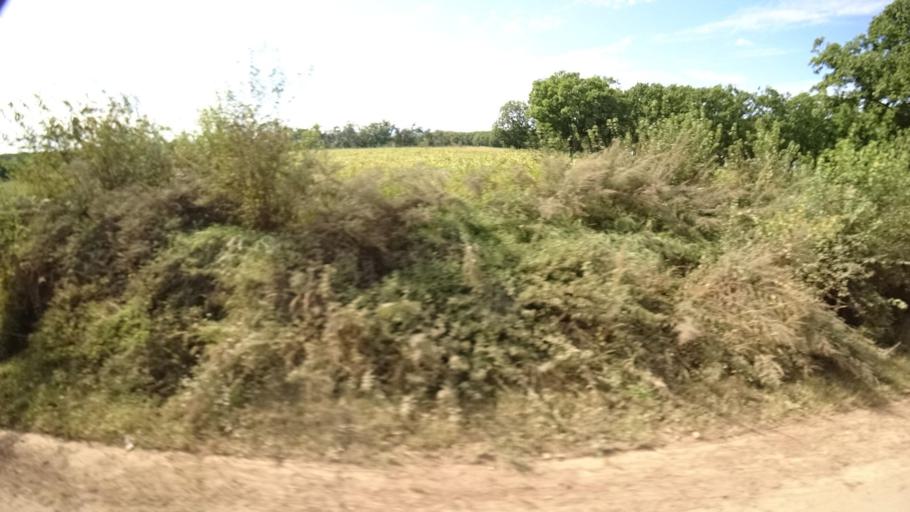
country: RU
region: Primorskiy
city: Dostoyevka
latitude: 44.3786
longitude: 133.5330
